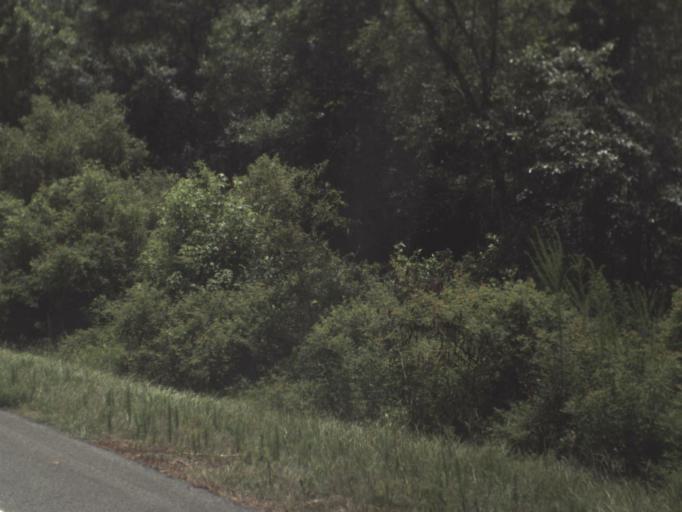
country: US
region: Florida
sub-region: Taylor County
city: Perry
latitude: 30.1164
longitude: -83.7250
